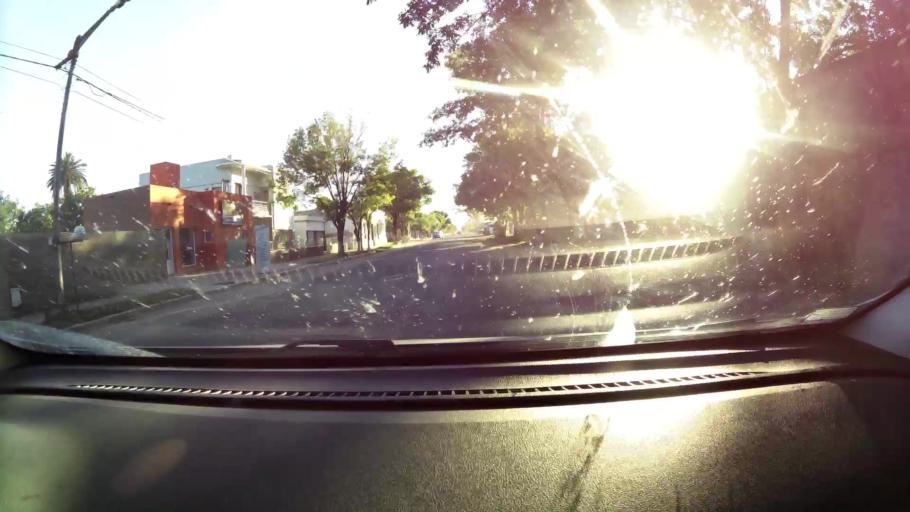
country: AR
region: Cordoba
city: Las Varas
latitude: -31.7989
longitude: -62.6157
